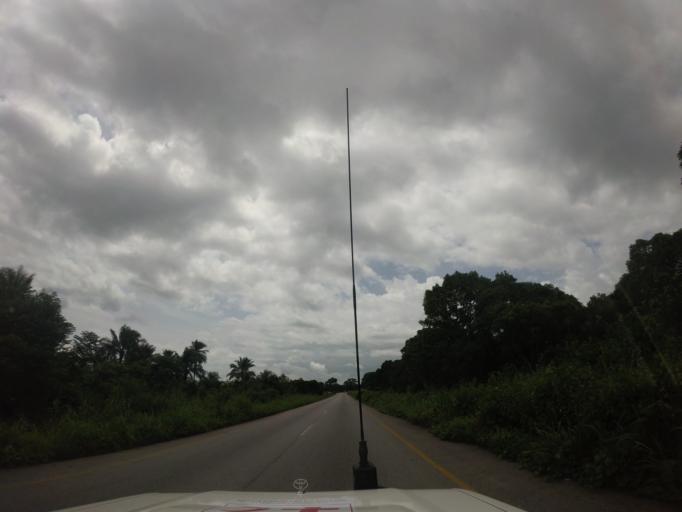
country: SL
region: Southern Province
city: Rotifunk
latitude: 8.4680
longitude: -12.6558
